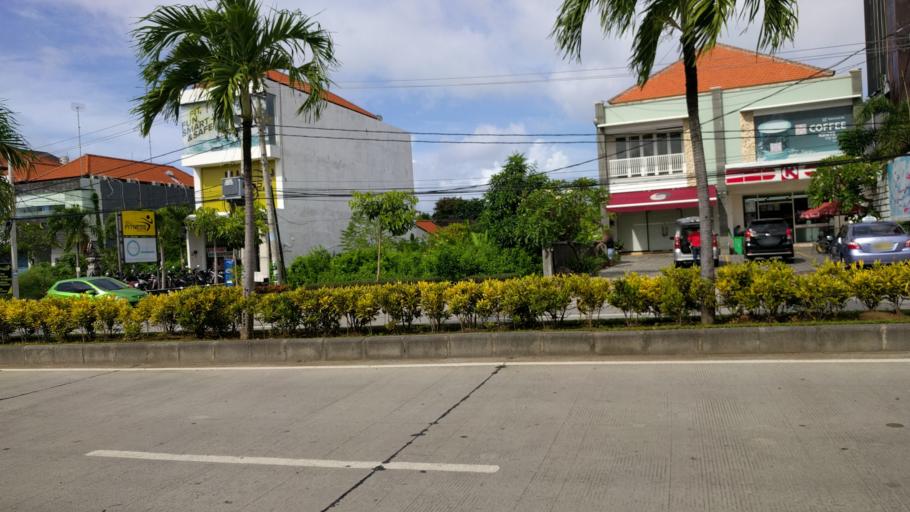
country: ID
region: Bali
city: Kuta
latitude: -8.6872
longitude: 115.1711
